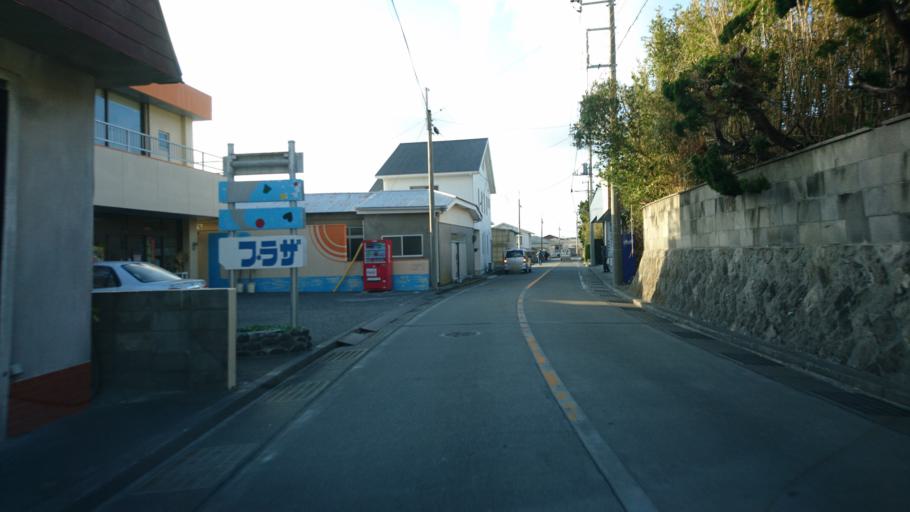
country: JP
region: Shizuoka
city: Shimoda
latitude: 34.3729
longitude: 139.2577
